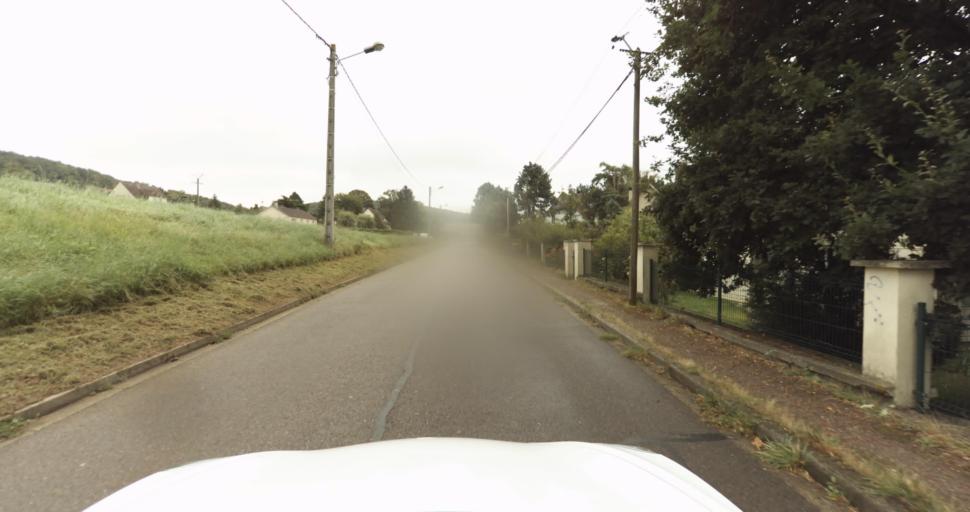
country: FR
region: Haute-Normandie
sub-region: Departement de l'Eure
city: Normanville
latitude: 49.0794
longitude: 1.1601
